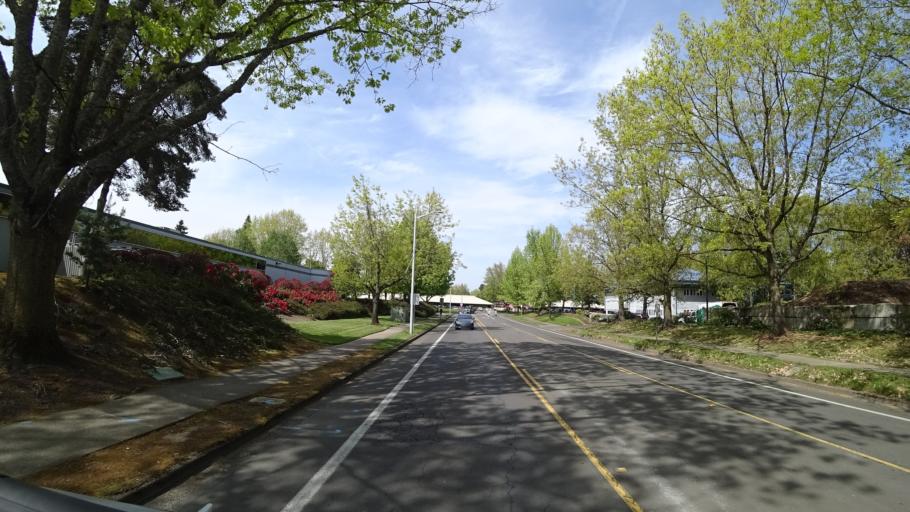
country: US
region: Oregon
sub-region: Washington County
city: Rockcreek
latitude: 45.5261
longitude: -122.9292
